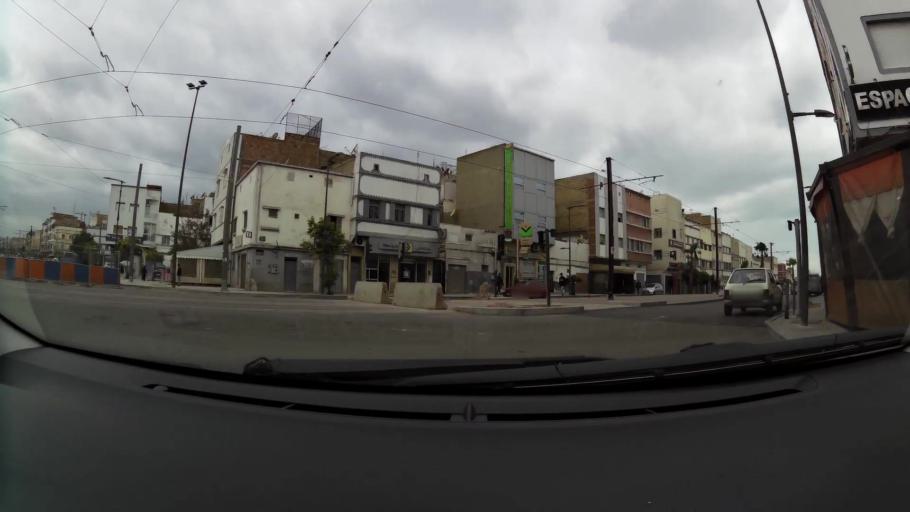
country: MA
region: Grand Casablanca
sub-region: Casablanca
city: Casablanca
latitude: 33.5822
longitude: -7.5618
